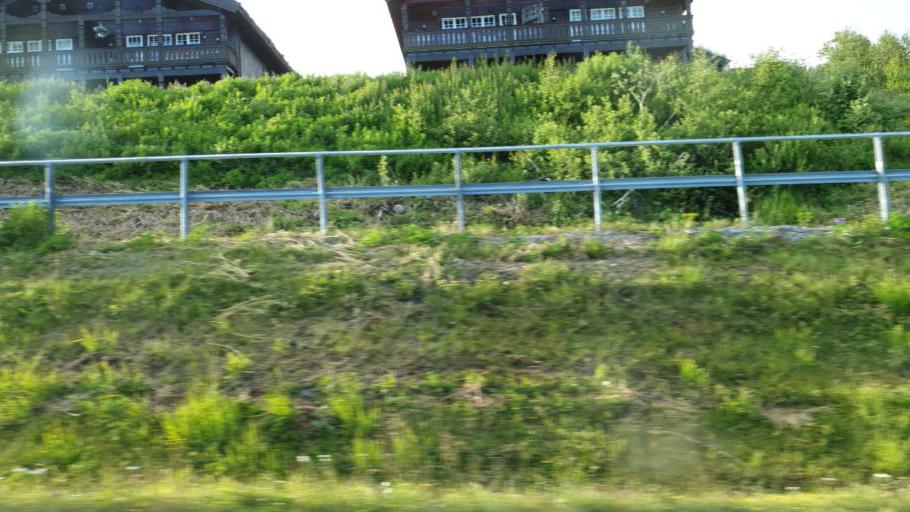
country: NO
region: Oppland
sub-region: Vestre Slidre
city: Slidre
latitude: 61.2502
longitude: 8.8944
